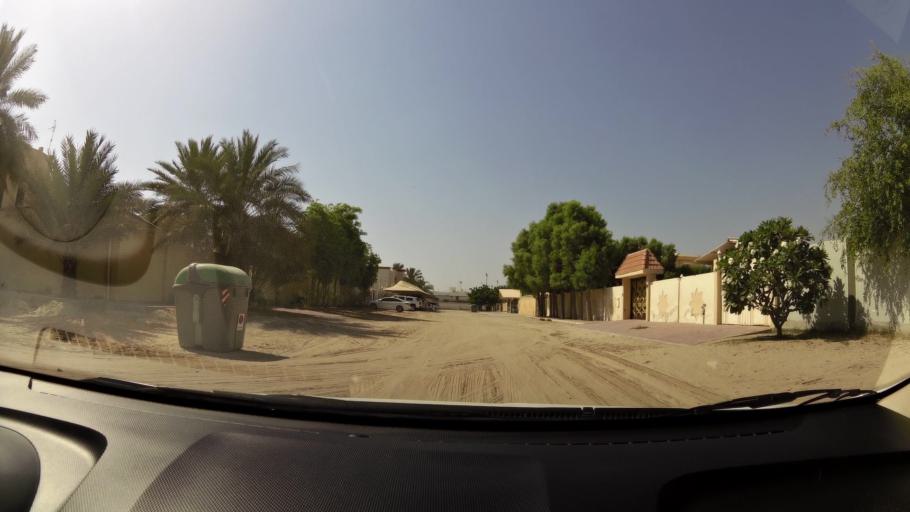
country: AE
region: Ajman
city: Ajman
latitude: 25.4202
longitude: 55.4693
